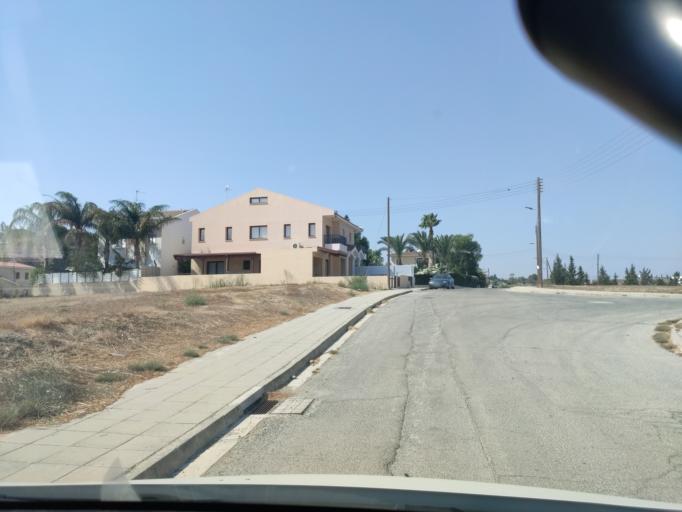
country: CY
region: Lefkosia
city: Geri
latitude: 35.1166
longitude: 33.4185
